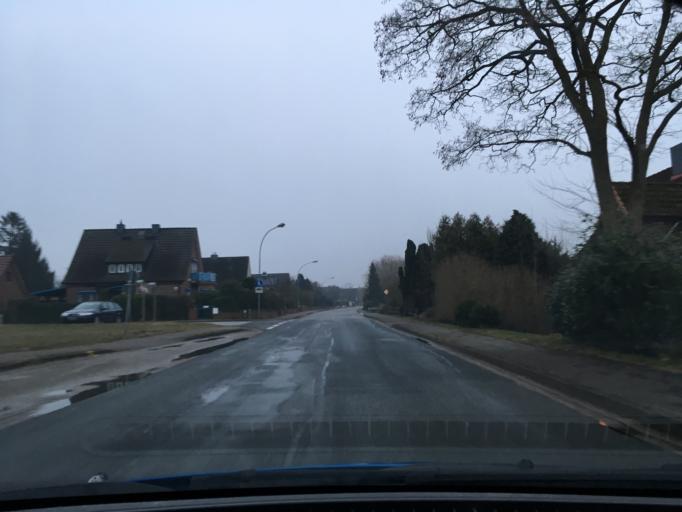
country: DE
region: Lower Saxony
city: Stelle
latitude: 53.4519
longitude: 10.0698
